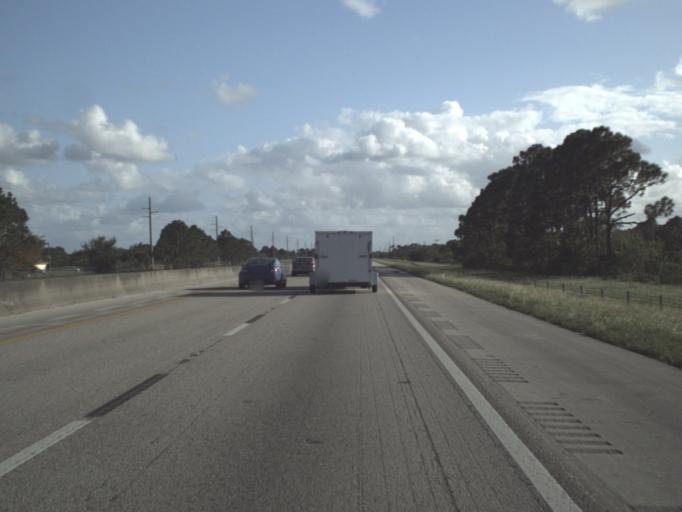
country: US
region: Florida
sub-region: Saint Lucie County
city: River Park
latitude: 27.3312
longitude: -80.3744
